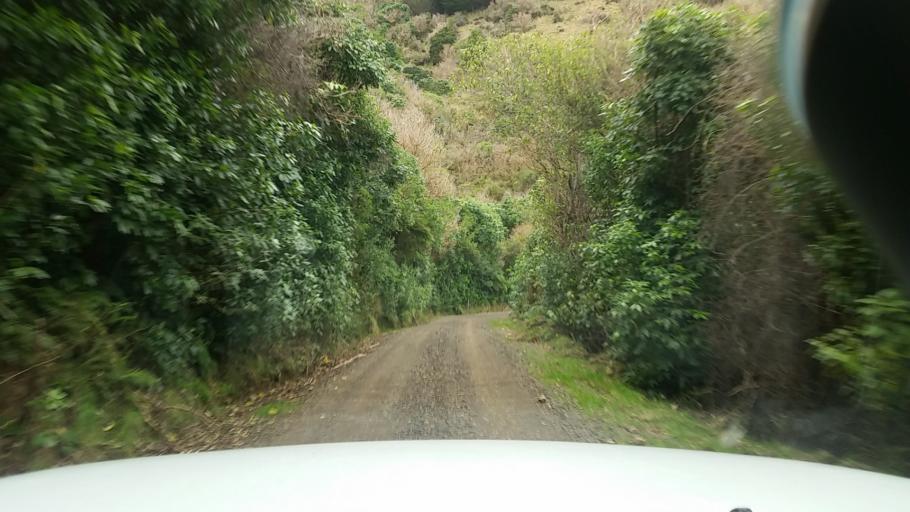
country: NZ
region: Canterbury
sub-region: Christchurch City
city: Christchurch
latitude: -43.7221
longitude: 172.7978
